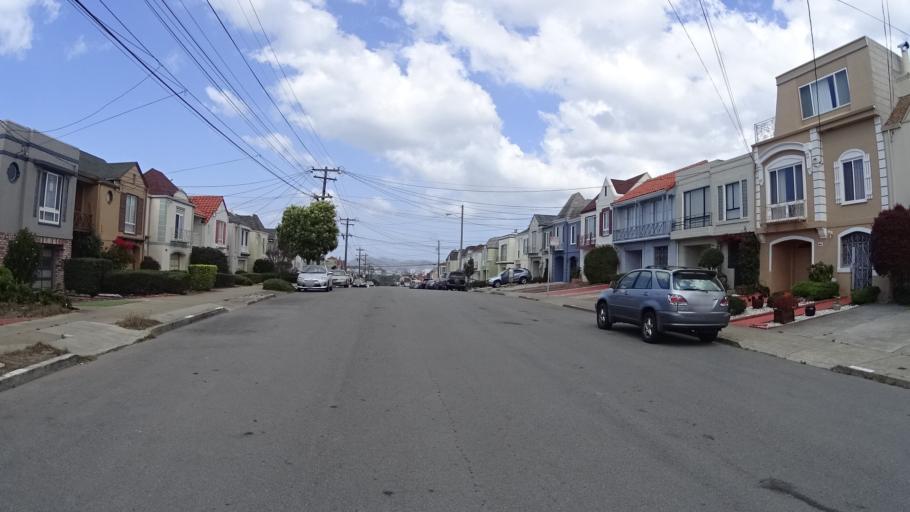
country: US
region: California
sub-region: San Mateo County
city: Daly City
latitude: 37.7562
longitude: -122.4917
